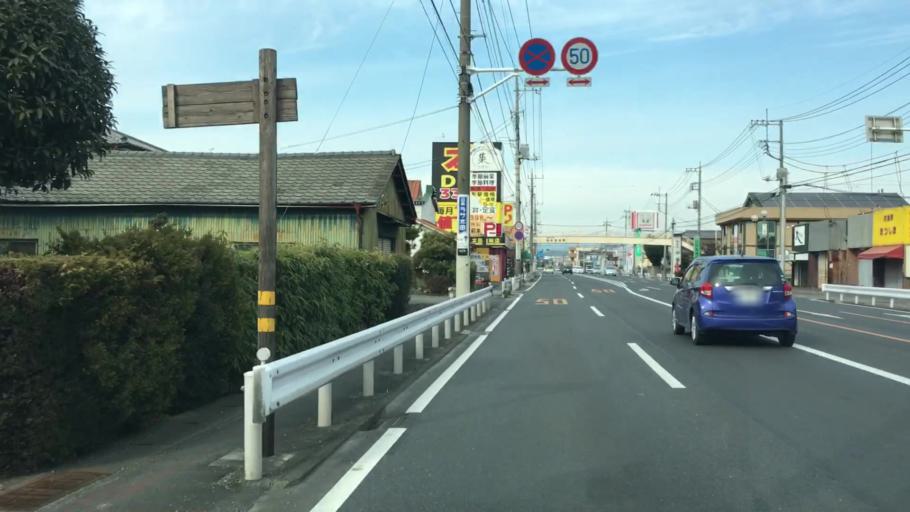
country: JP
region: Saitama
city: Menuma
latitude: 36.2542
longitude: 139.3780
